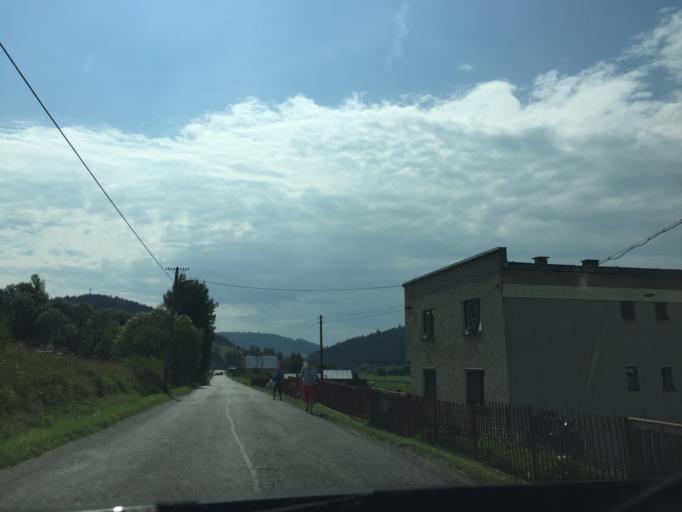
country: PL
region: Silesian Voivodeship
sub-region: Powiat zywiecki
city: Sopotnia Wielka
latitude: 49.4416
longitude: 19.3115
